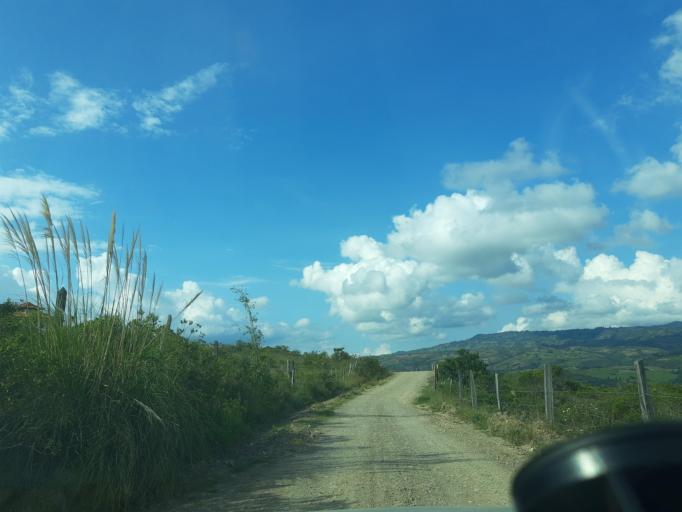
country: CO
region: Boyaca
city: Villa de Leiva
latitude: 5.6652
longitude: -73.5537
